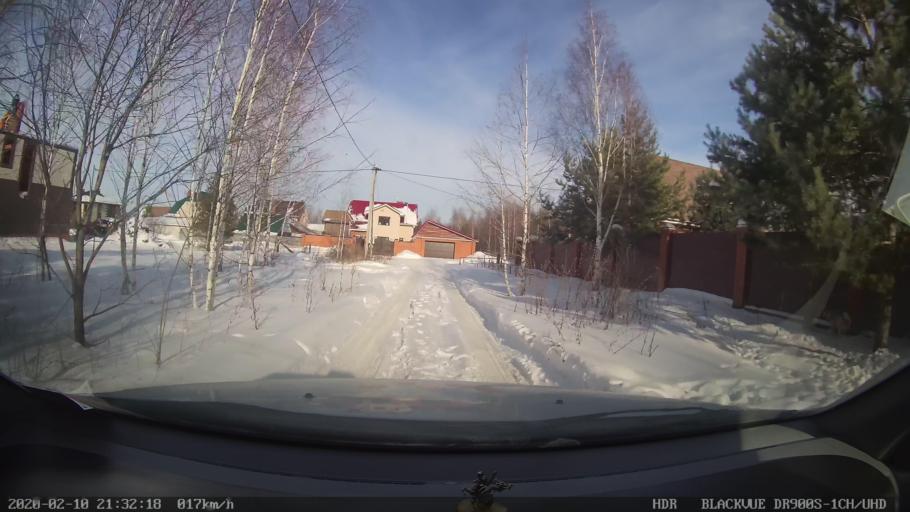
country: RU
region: Tatarstan
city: Vysokaya Gora
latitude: 55.7792
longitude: 49.2762
